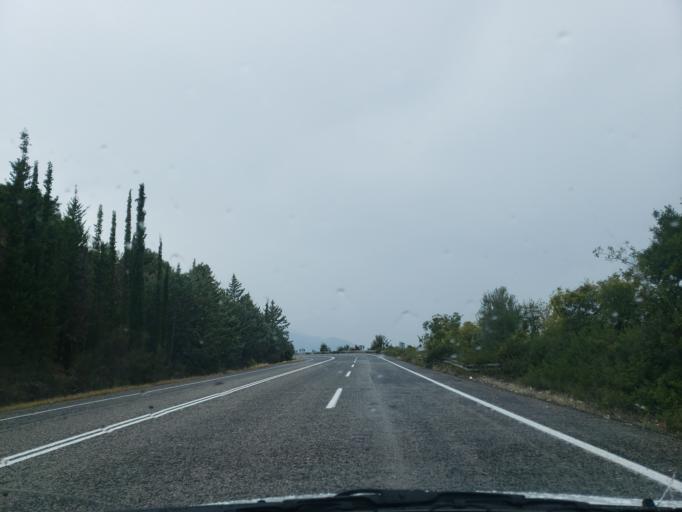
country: GR
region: Central Greece
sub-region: Nomos Fthiotidos
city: Anthili
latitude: 38.7939
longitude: 22.4781
